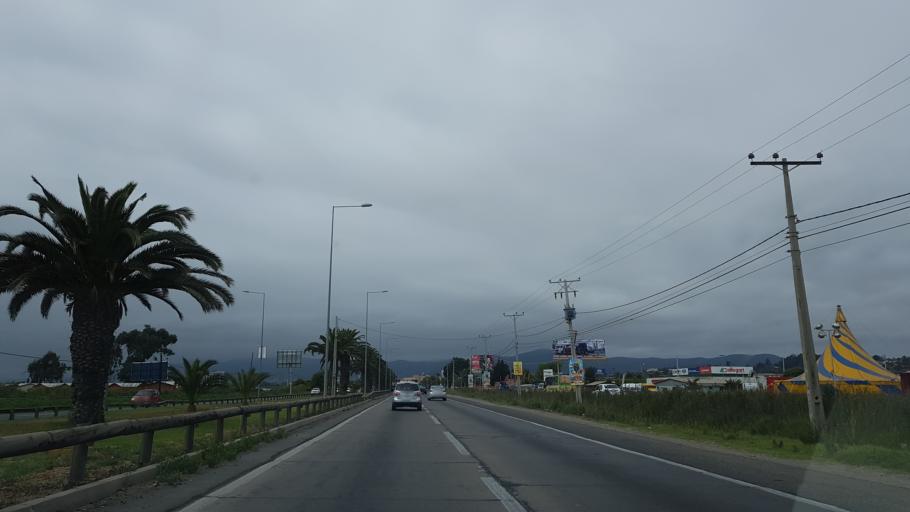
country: CL
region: Coquimbo
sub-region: Provincia de Elqui
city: La Serena
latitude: -29.9219
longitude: -71.2658
